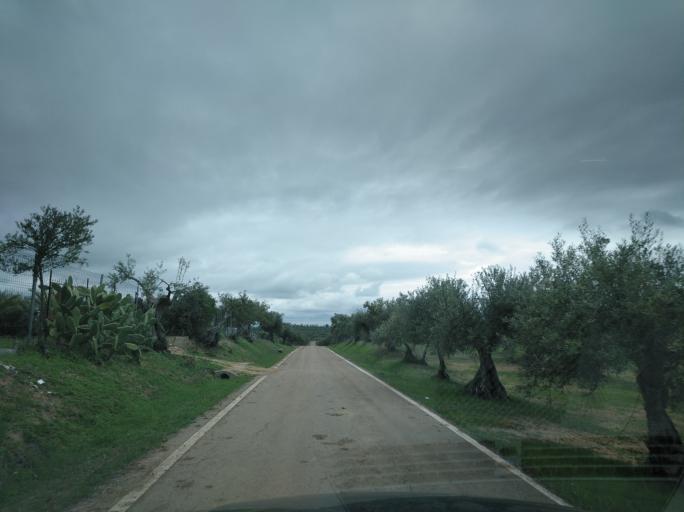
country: PT
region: Portalegre
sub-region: Campo Maior
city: Campo Maior
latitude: 38.9838
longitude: -7.0367
